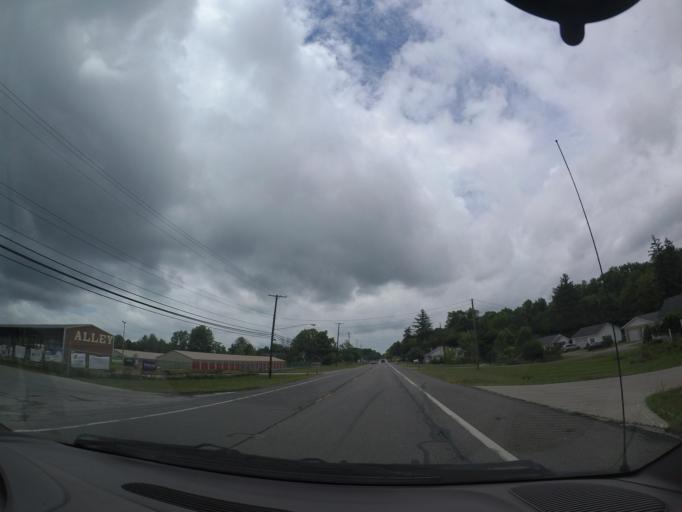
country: US
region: Ohio
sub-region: Ashtabula County
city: Geneva
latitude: 41.7779
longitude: -80.9467
